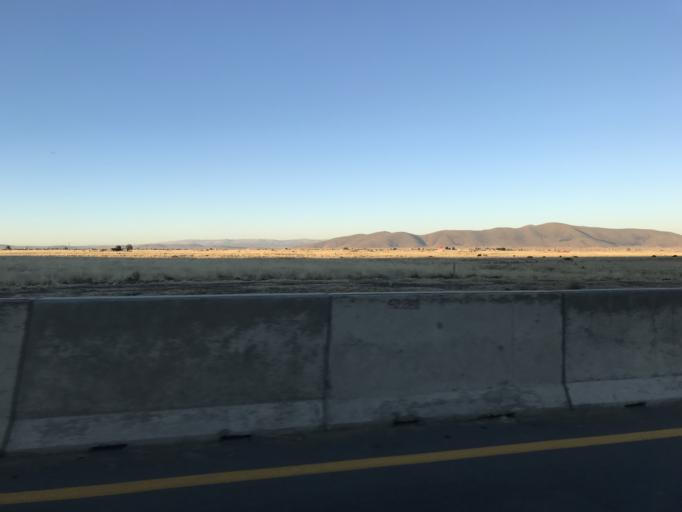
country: BO
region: La Paz
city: Batallas
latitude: -16.2990
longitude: -68.5137
